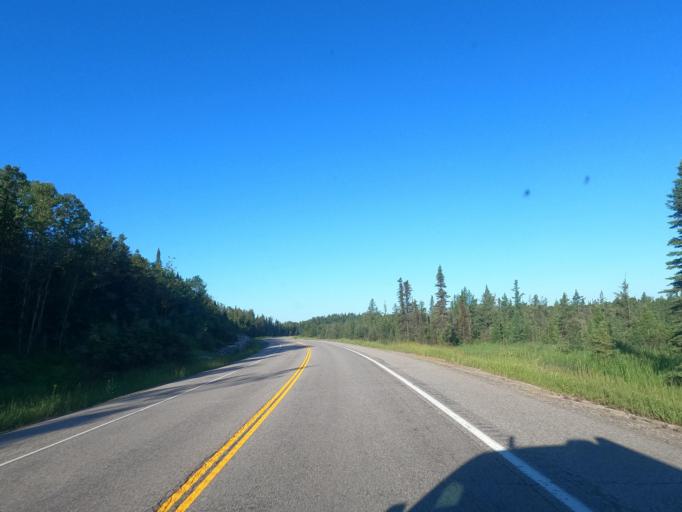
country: CA
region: Ontario
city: Dryden
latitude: 49.8318
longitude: -93.5893
